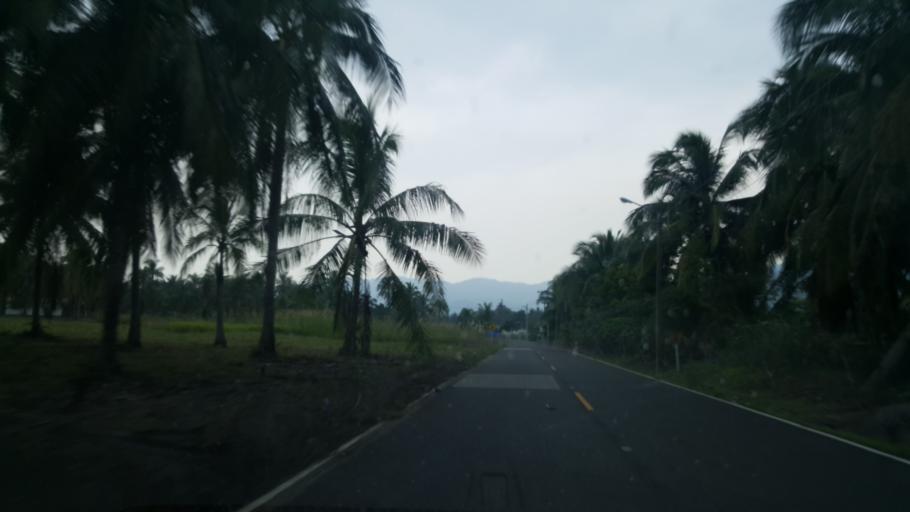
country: TH
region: Chon Buri
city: Ban Bueng
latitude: 13.2301
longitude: 101.0349
